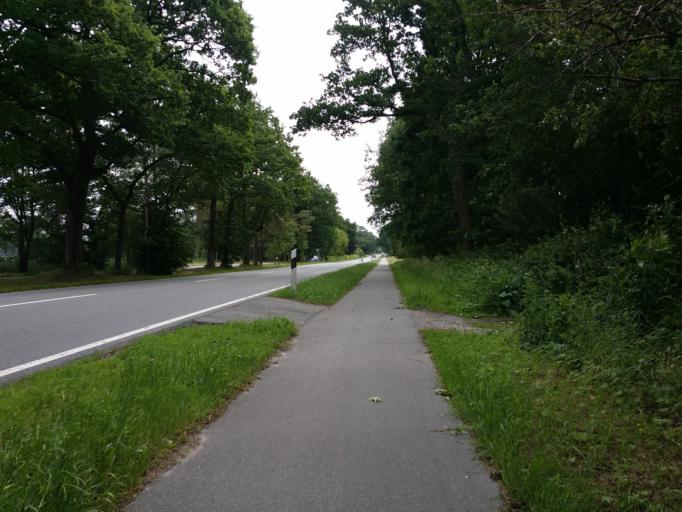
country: DE
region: Lower Saxony
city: Zetel
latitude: 53.3980
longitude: 7.9217
